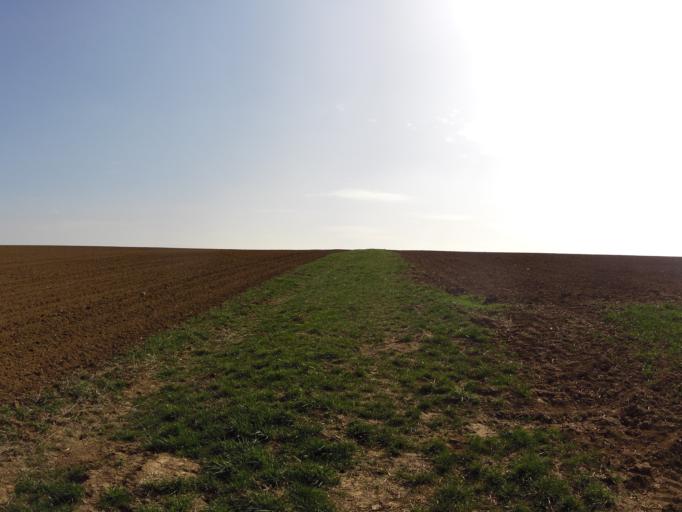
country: DE
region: Bavaria
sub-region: Regierungsbezirk Unterfranken
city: Mainstockheim
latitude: 49.7923
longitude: 10.1414
